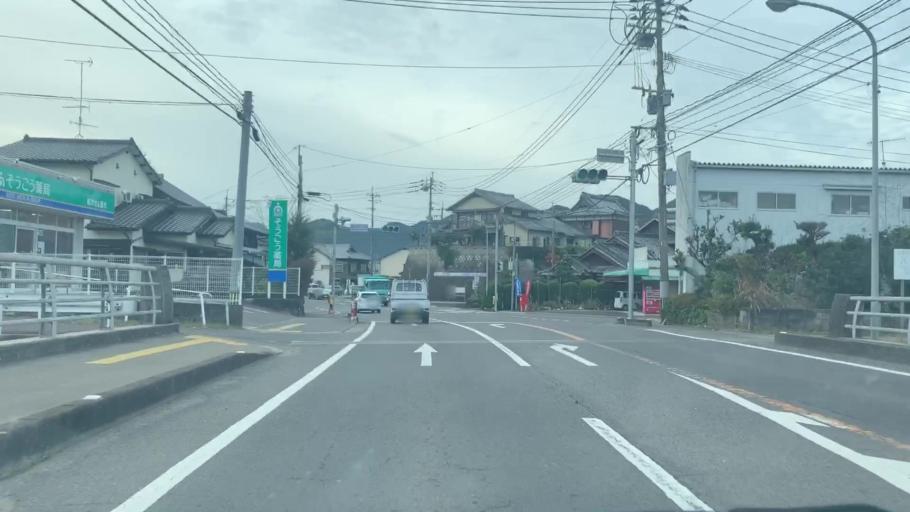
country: JP
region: Saga Prefecture
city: Kashima
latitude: 33.1327
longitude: 130.0616
